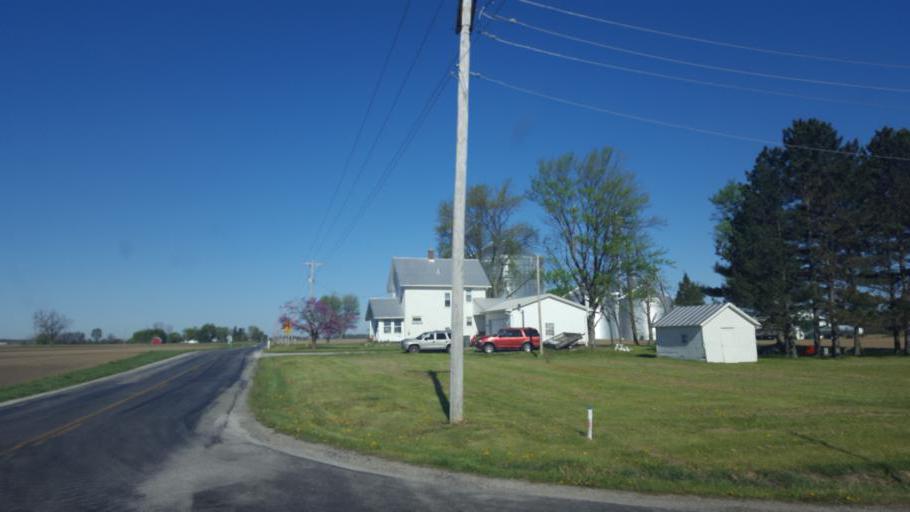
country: US
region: Ohio
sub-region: Marion County
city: Marion
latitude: 40.6739
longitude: -83.0686
